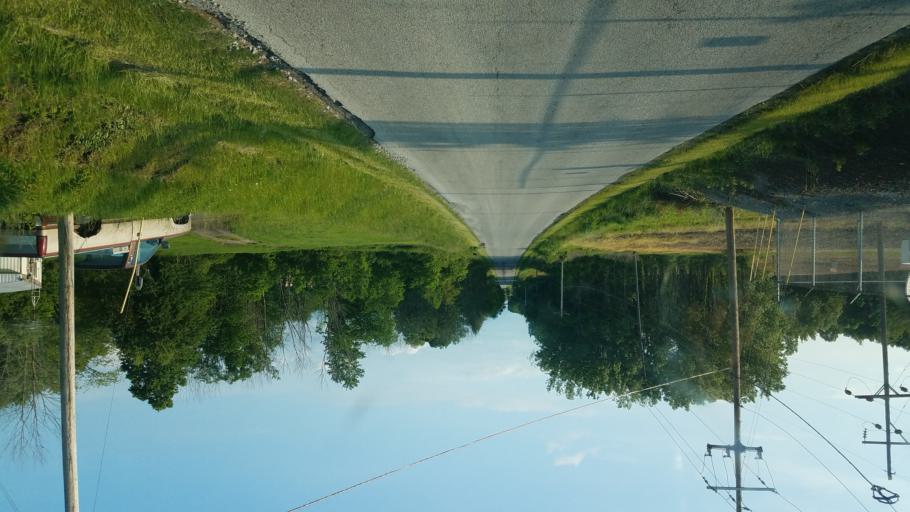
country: US
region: Ohio
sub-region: Morrow County
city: Cardington
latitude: 40.4239
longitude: -82.7868
